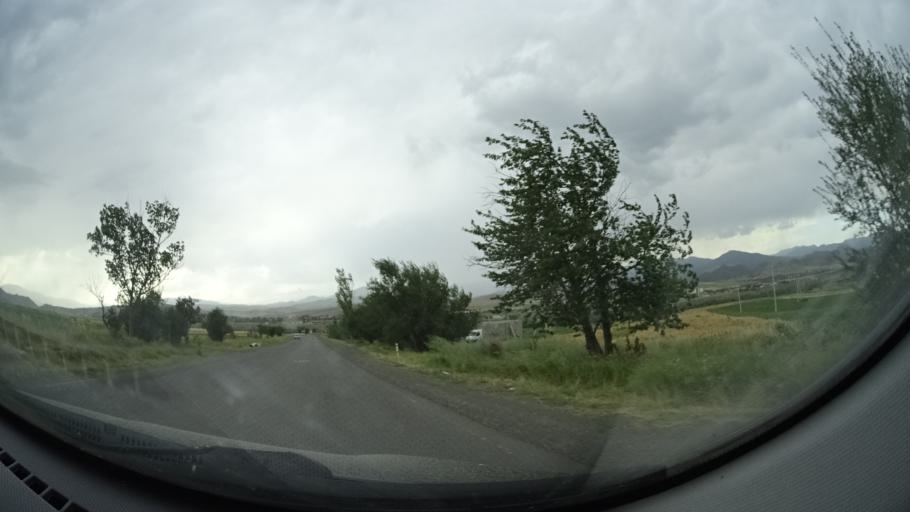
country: GE
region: Samtskhe-Javakheti
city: Akhaltsikhe
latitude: 41.6407
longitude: 43.0285
